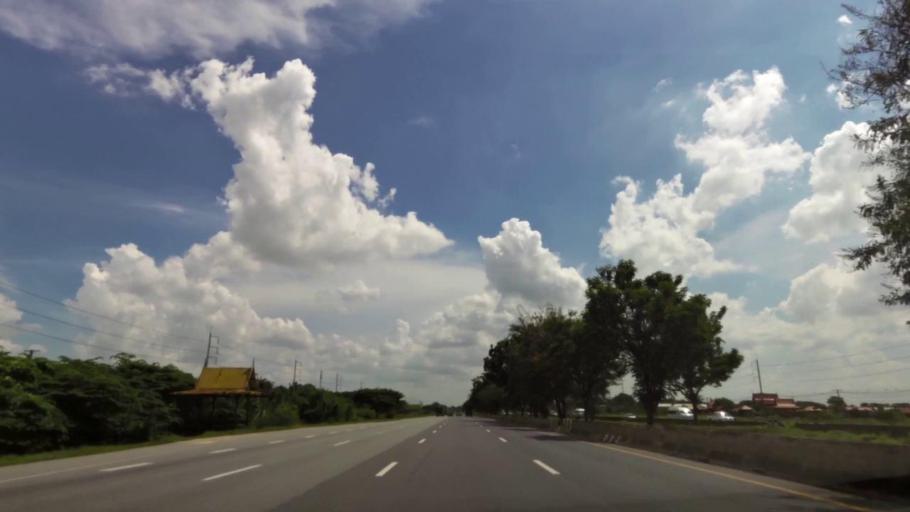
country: TH
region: Phra Nakhon Si Ayutthaya
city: Maha Rat
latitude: 14.5017
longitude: 100.5214
